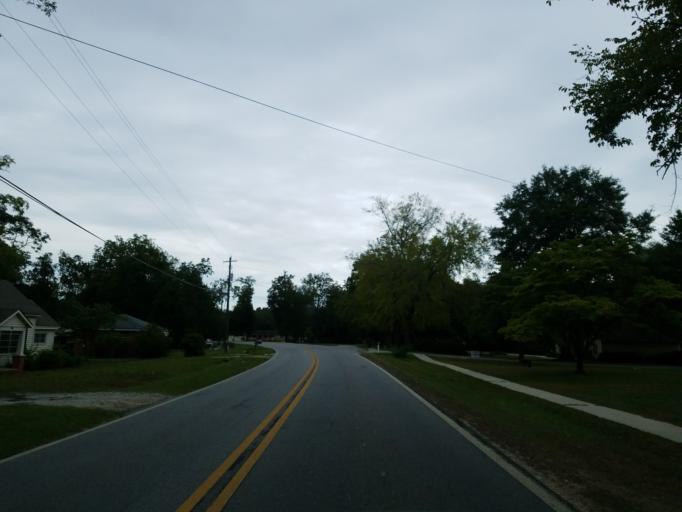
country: US
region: Georgia
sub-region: Lamar County
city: Barnesville
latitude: 33.1120
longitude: -84.1960
